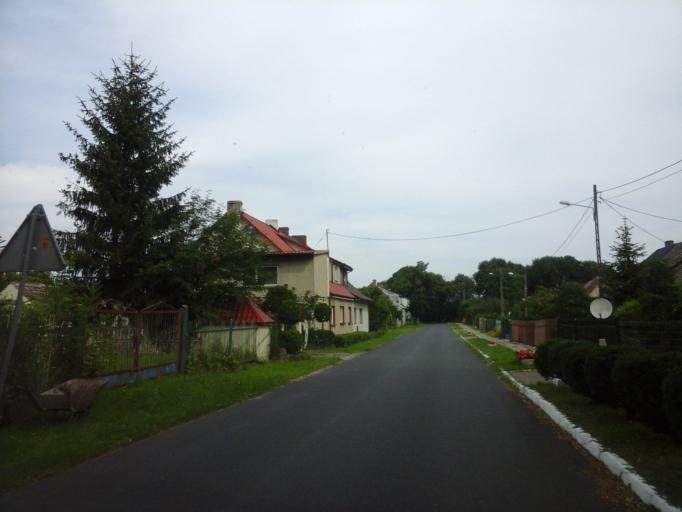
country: PL
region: West Pomeranian Voivodeship
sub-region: Powiat choszczenski
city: Recz
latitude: 53.2212
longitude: 15.6088
